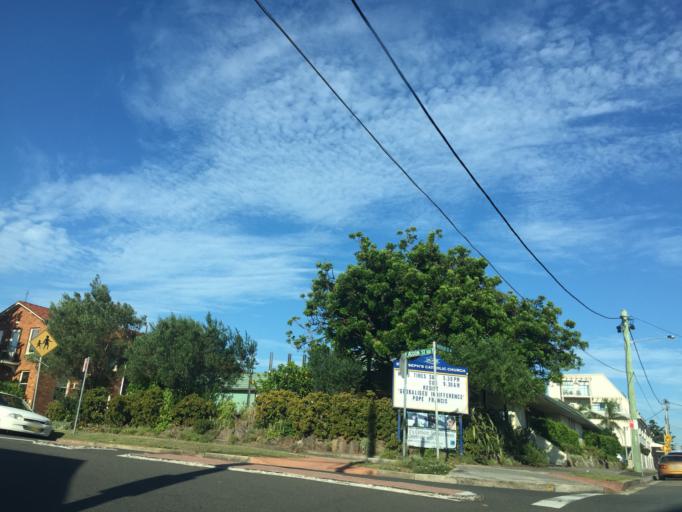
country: AU
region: New South Wales
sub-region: Warringah
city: Narrabeen
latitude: -33.7130
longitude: 151.2983
